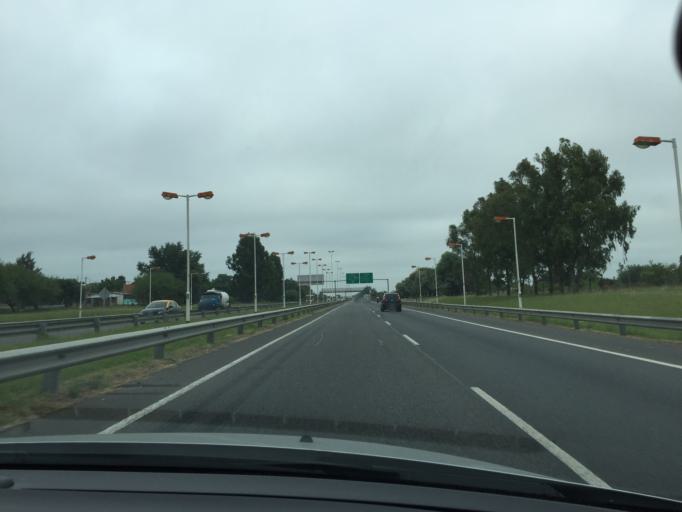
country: AR
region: Buenos Aires
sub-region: Partido de Ezeiza
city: Ezeiza
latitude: -34.8402
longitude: -58.5251
